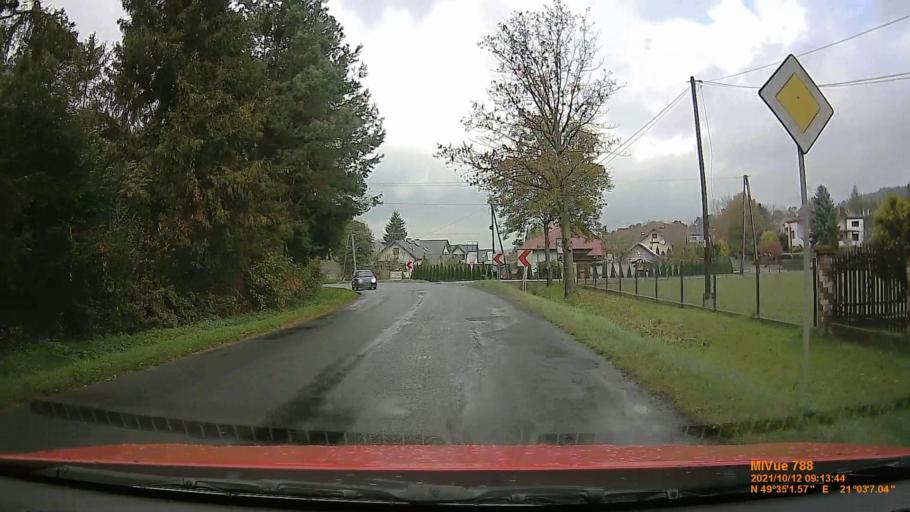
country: PL
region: Lesser Poland Voivodeship
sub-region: Powiat gorlicki
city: Ropa
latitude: 49.5839
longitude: 21.0519
